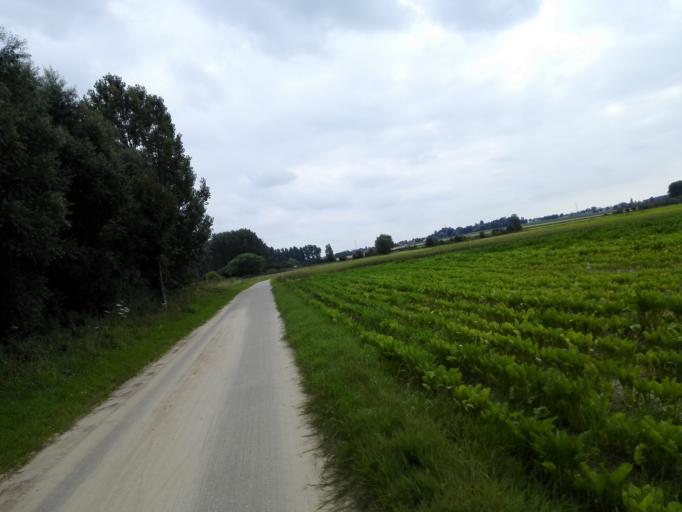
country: BE
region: Flanders
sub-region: Provincie Vlaams-Brabant
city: Tienen
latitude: 50.8095
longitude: 4.9915
